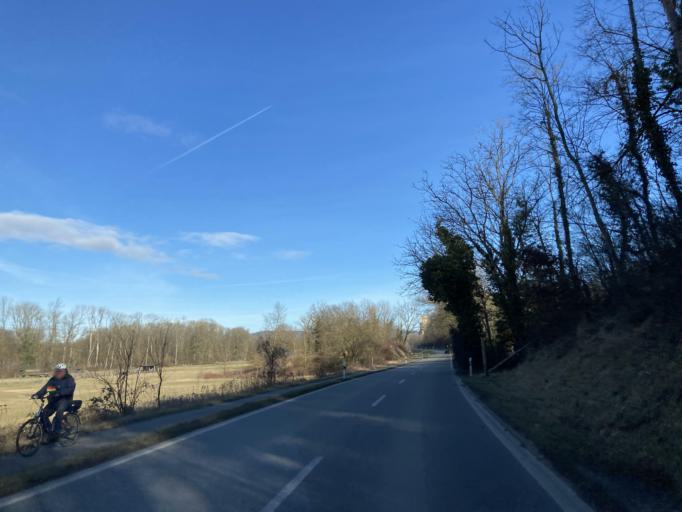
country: DE
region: Baden-Wuerttemberg
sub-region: Freiburg Region
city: Merdingen
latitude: 48.0029
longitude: 7.6695
